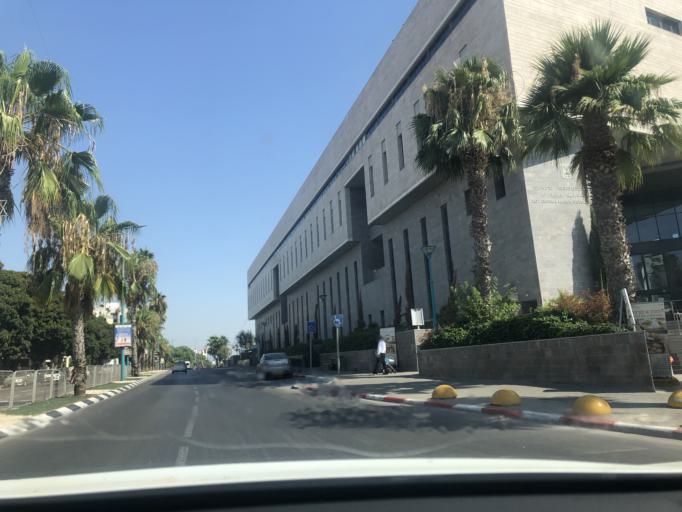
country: IL
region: Central District
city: Lod
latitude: 31.9464
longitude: 34.8925
